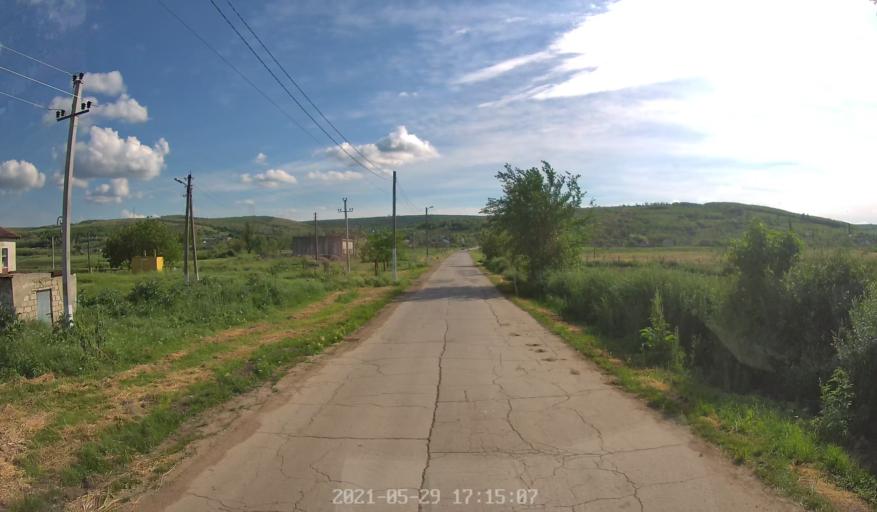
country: MD
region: Laloveni
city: Ialoveni
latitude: 46.8333
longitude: 28.8473
